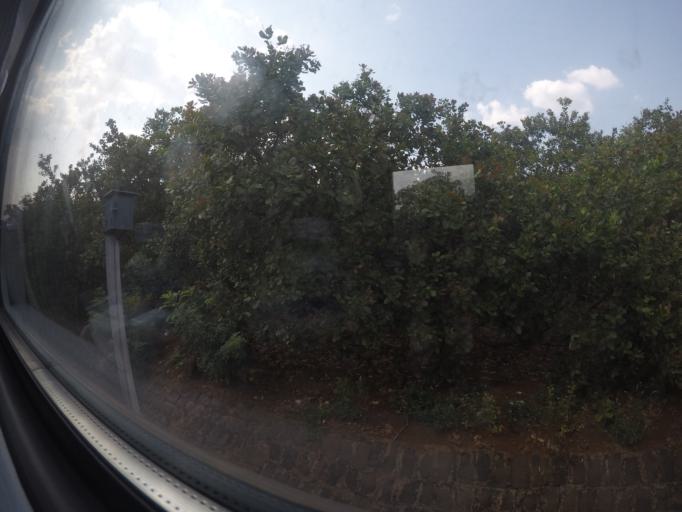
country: VN
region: Dong Nai
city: Thong Nhat
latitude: 10.9310
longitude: 107.1429
